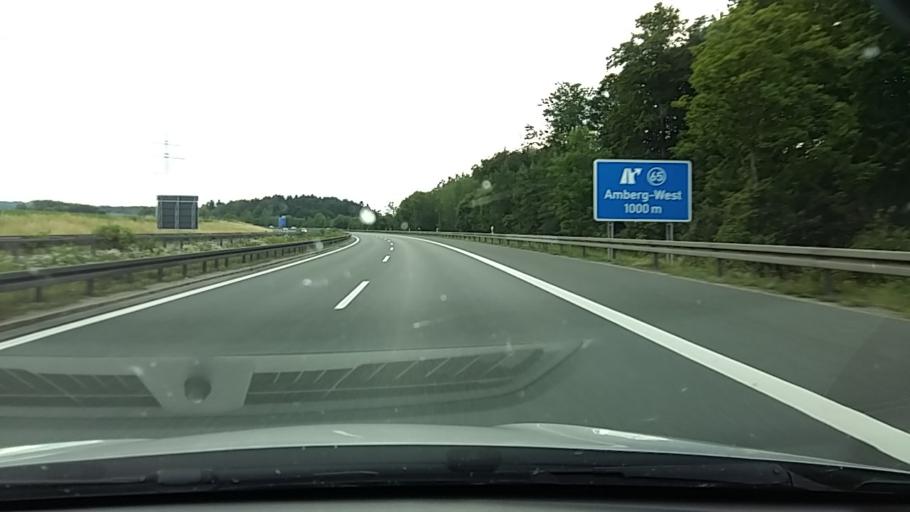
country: DE
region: Bavaria
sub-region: Upper Palatinate
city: Ursensollen
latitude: 49.4057
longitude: 11.7810
